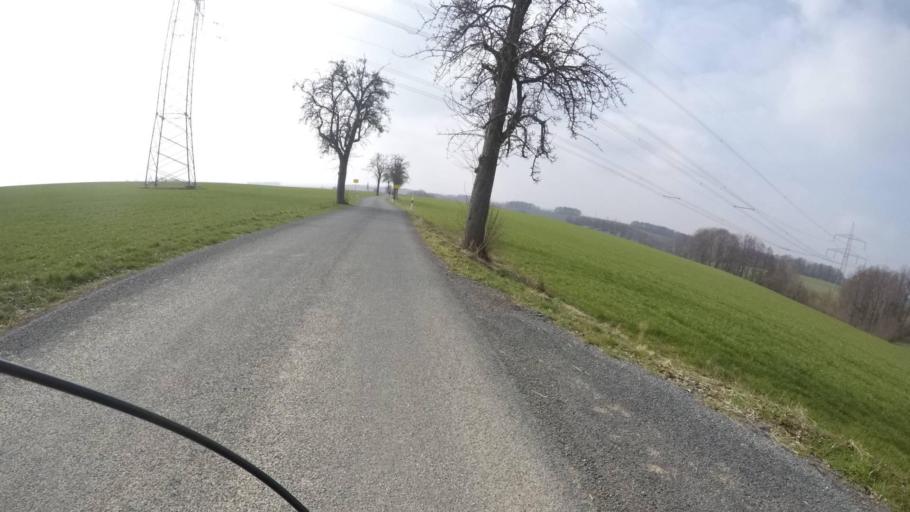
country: DE
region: Saxony
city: Niederfrohna
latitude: 50.8781
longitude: 12.6961
